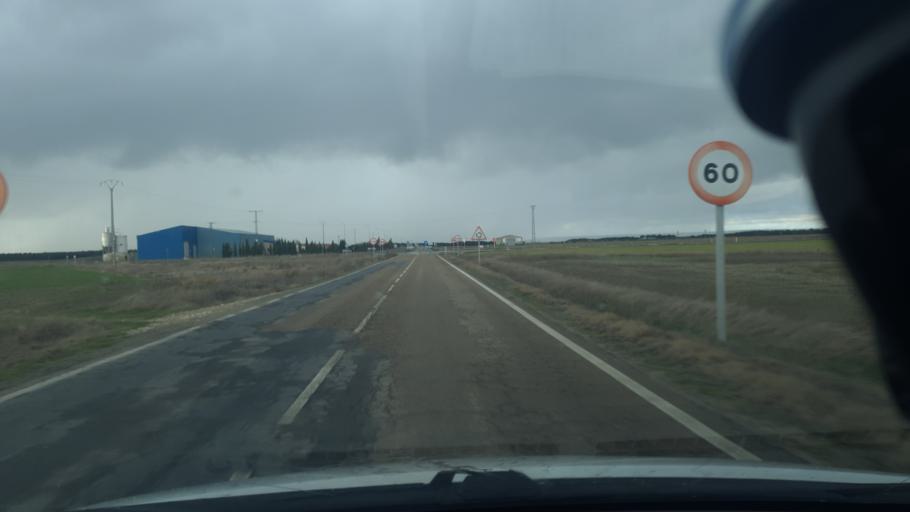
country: ES
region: Castille and Leon
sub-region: Provincia de Segovia
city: Chane
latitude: 41.3182
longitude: -4.3846
